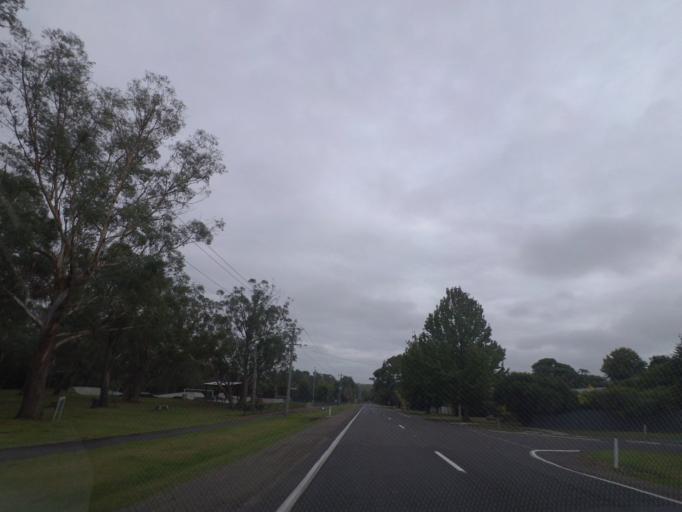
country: AU
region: Victoria
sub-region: Yarra Ranges
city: Healesville
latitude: -37.6563
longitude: 145.5270
